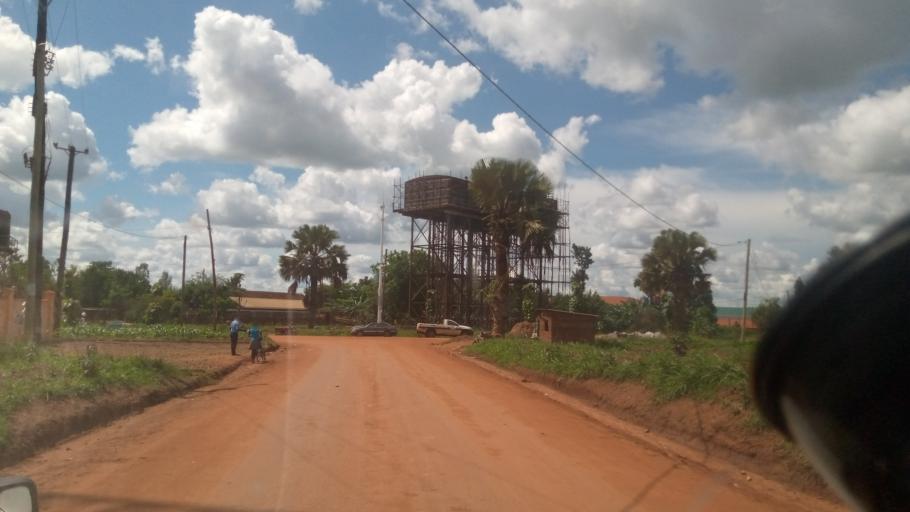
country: UG
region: Northern Region
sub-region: Lira District
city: Lira
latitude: 2.2354
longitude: 32.9042
